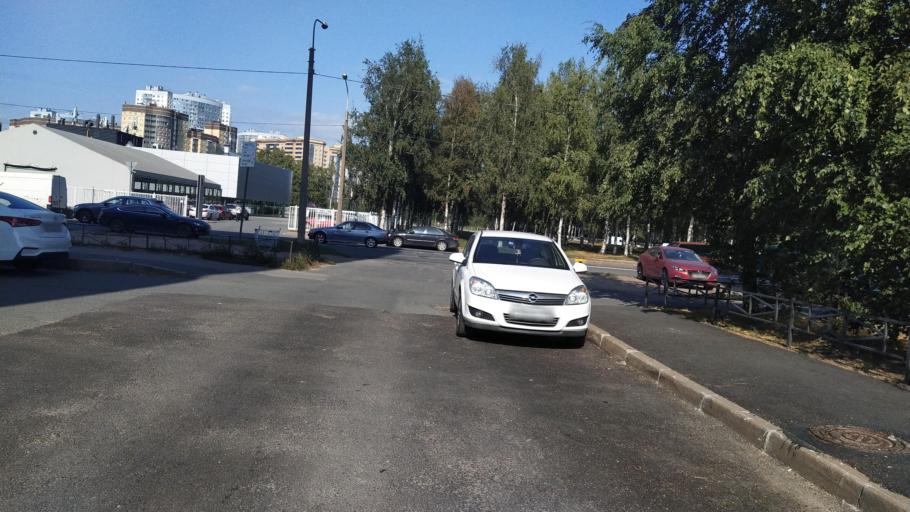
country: RU
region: Leningrad
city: Untolovo
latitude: 59.9913
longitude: 30.2152
